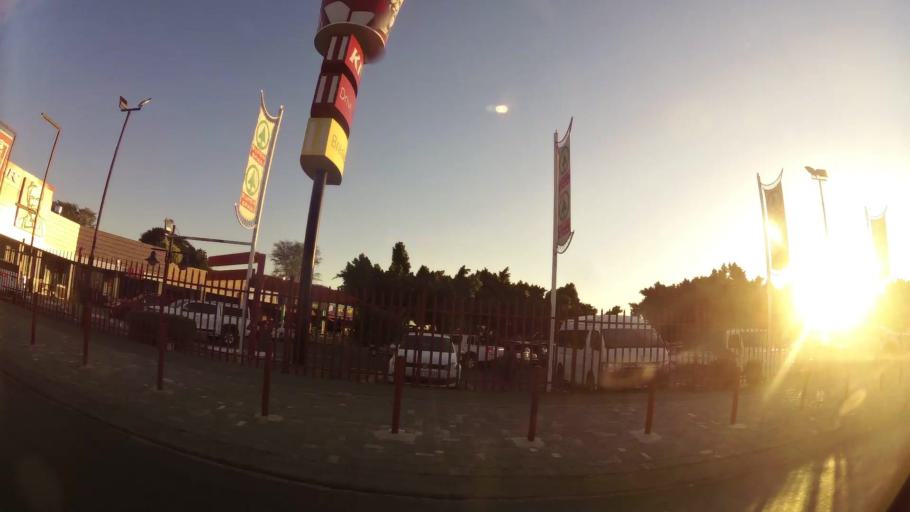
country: ZA
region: North-West
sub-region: Bojanala Platinum District Municipality
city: Rustenburg
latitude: -25.6942
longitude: 27.2253
